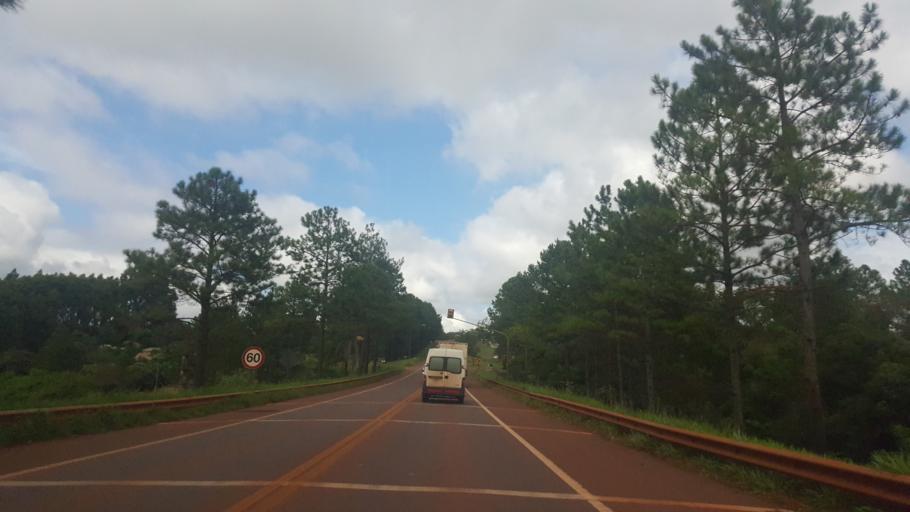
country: AR
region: Misiones
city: Aristobulo del Valle
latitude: -27.0844
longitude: -54.8237
